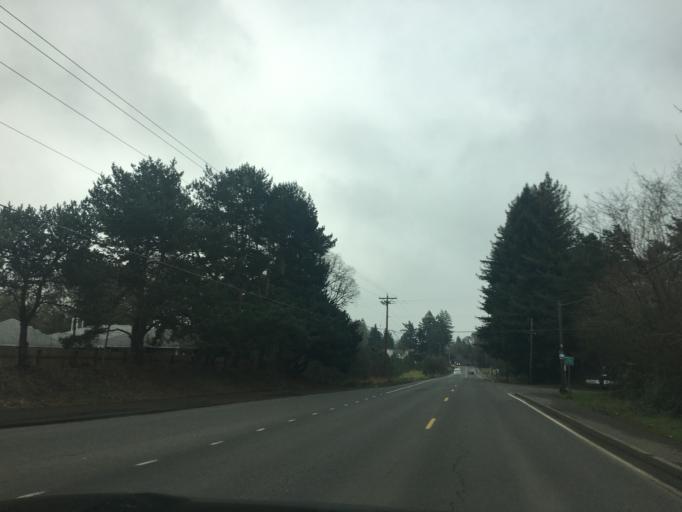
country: US
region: Oregon
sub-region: Washington County
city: Aloha
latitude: 45.4708
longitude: -122.8788
